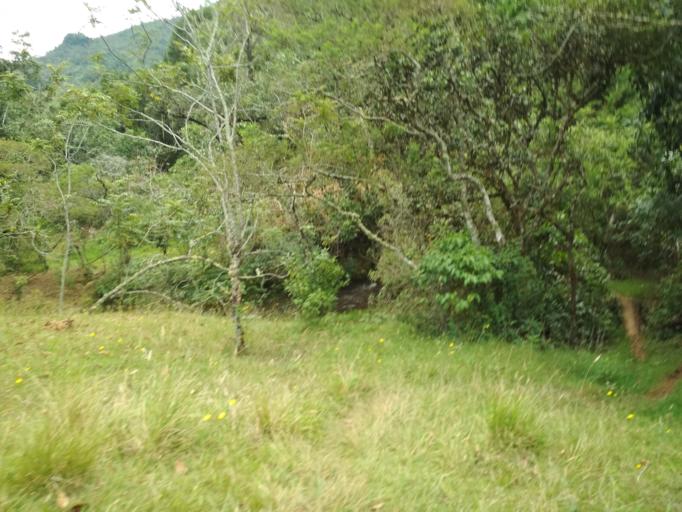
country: CO
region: Cauca
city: Totoro
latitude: 2.5328
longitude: -76.4204
